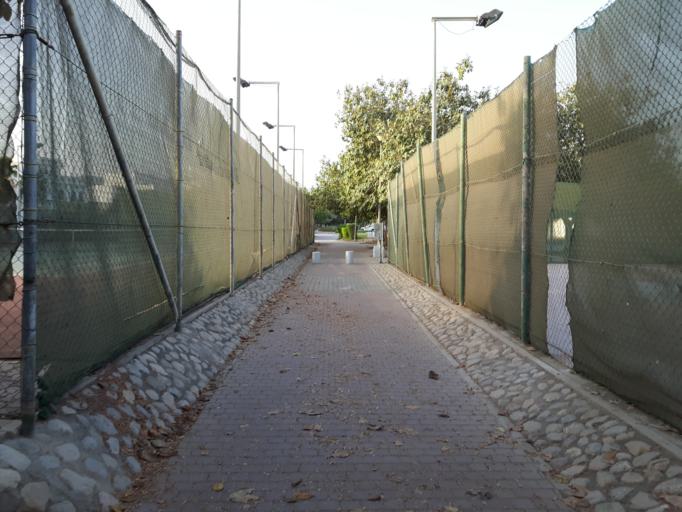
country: OM
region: Muhafazat Masqat
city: Bawshar
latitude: 23.6150
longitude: 58.4620
